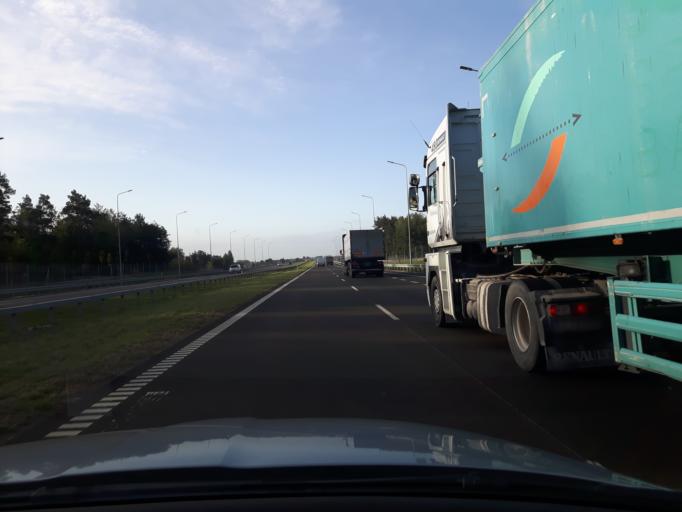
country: PL
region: Masovian Voivodeship
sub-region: Powiat radomski
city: Zakrzew
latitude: 51.4375
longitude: 21.0334
